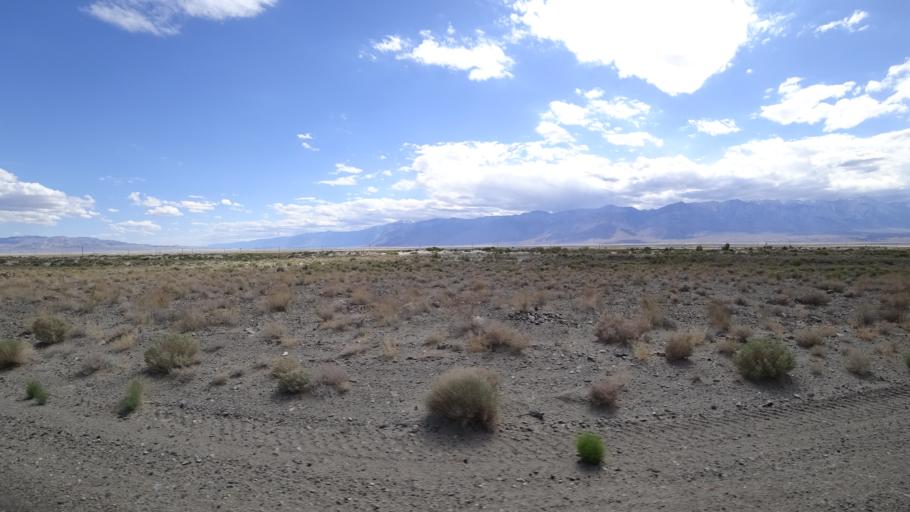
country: US
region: California
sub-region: Inyo County
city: Lone Pine
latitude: 36.5265
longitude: -117.9079
